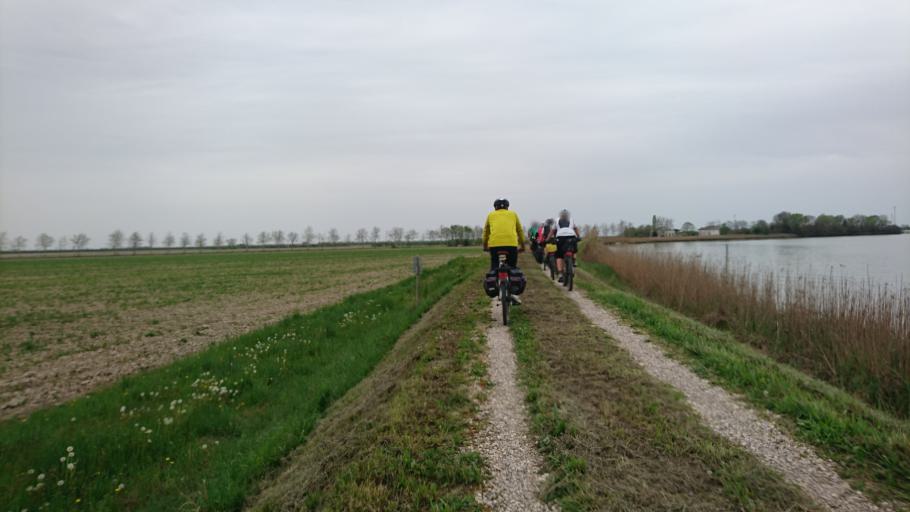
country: IT
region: Veneto
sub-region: Provincia di Venezia
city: Lugugnana
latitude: 45.6752
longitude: 12.9630
